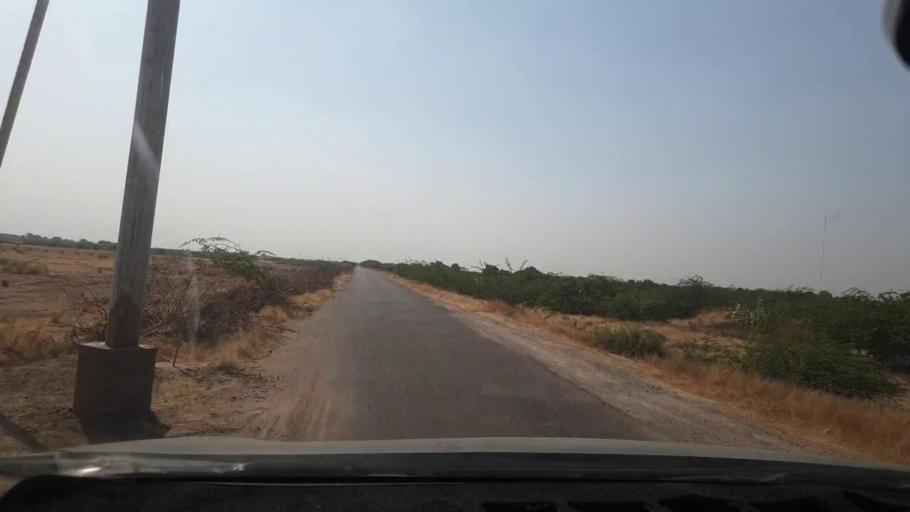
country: PK
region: Sindh
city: Malir Cantonment
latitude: 25.1075
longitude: 67.2016
